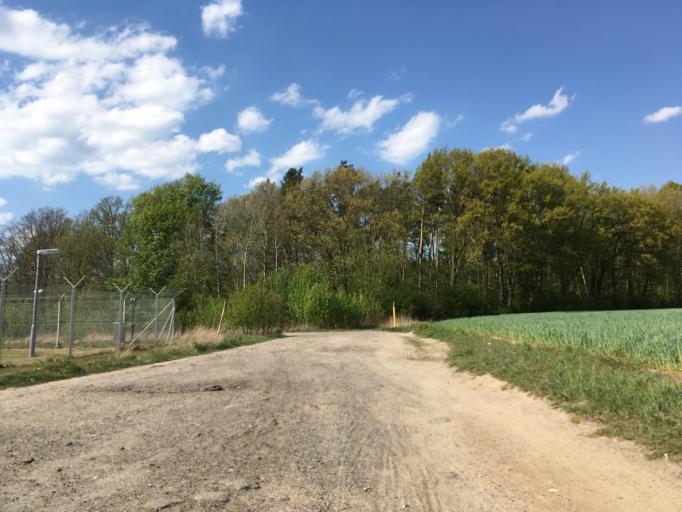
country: DE
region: Brandenburg
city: Ahrensfelde
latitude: 52.6022
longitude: 13.5771
